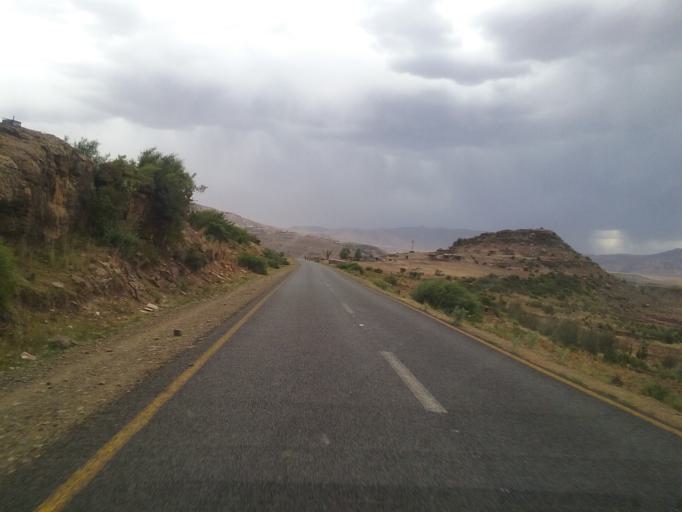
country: LS
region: Quthing
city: Quthing
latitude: -30.2890
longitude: 27.8088
